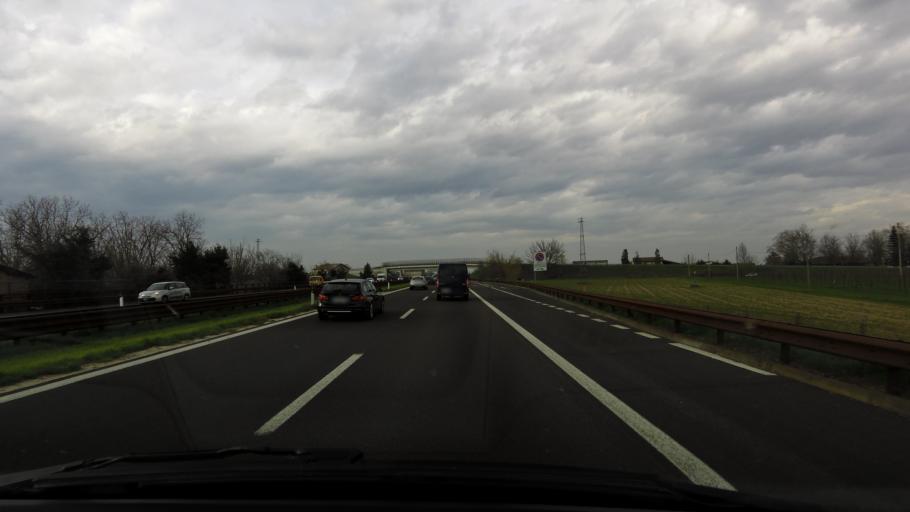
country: IT
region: Emilia-Romagna
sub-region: Provincia di Modena
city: Santa Croce Scuole
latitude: 44.7327
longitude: 10.8442
